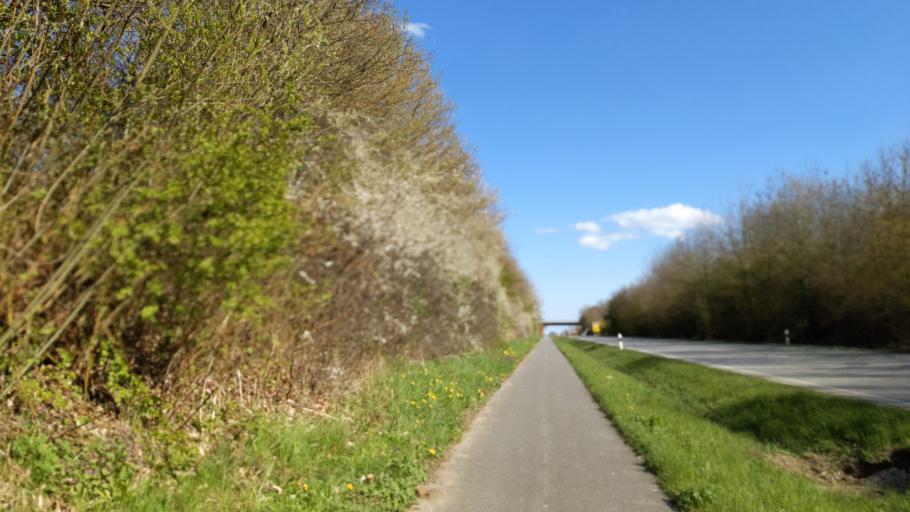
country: DE
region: Schleswig-Holstein
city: Eutin
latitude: 54.1199
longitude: 10.6087
